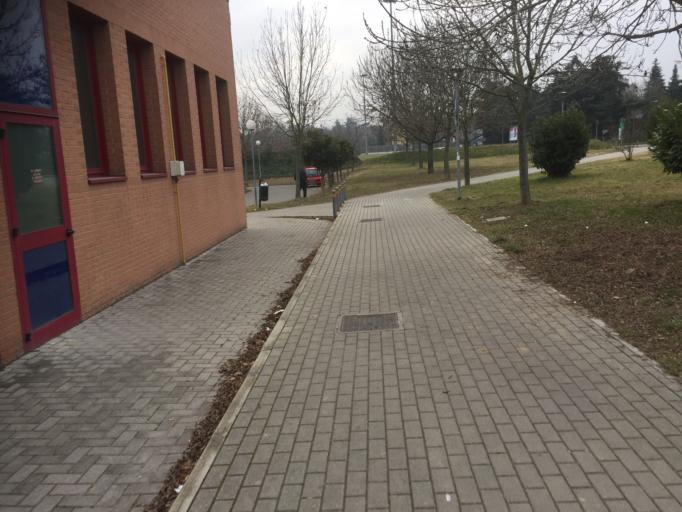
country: IT
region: Emilia-Romagna
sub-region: Provincia di Bologna
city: San Lazzaro
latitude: 44.4706
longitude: 11.3931
